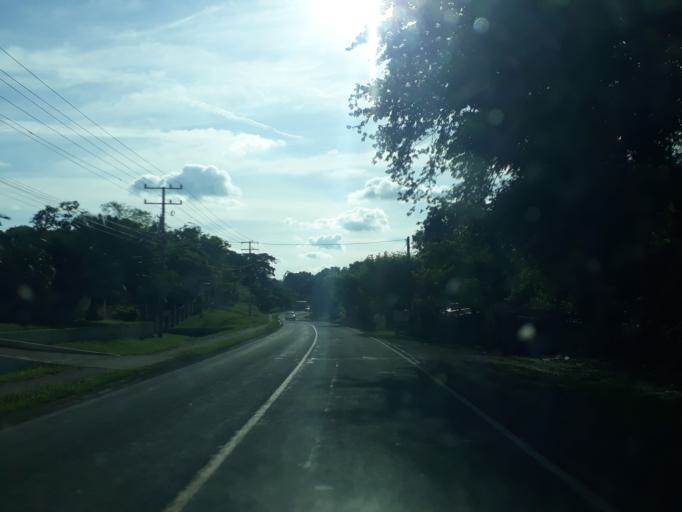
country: NI
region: Masaya
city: Masatepe
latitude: 11.9047
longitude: -86.1596
